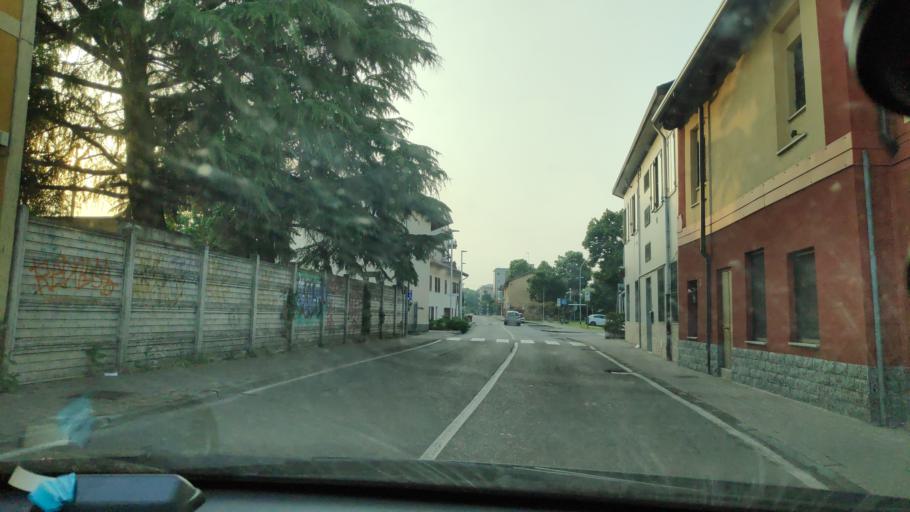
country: IT
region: Lombardy
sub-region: Citta metropolitana di Milano
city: Rozzano
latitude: 45.3745
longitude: 9.1469
